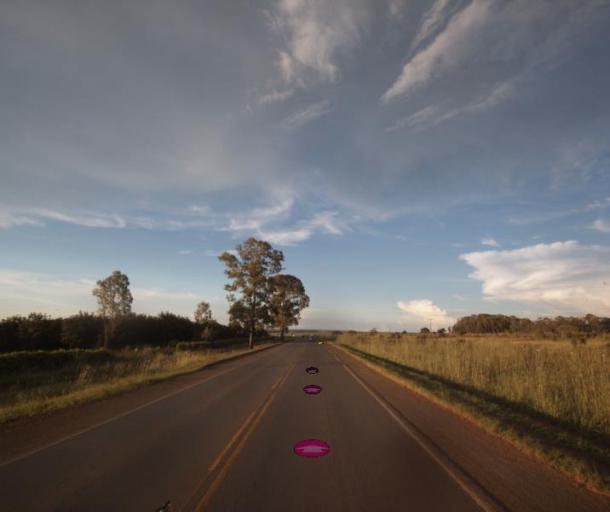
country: BR
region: Goias
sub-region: Anapolis
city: Anapolis
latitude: -16.2017
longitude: -48.9108
